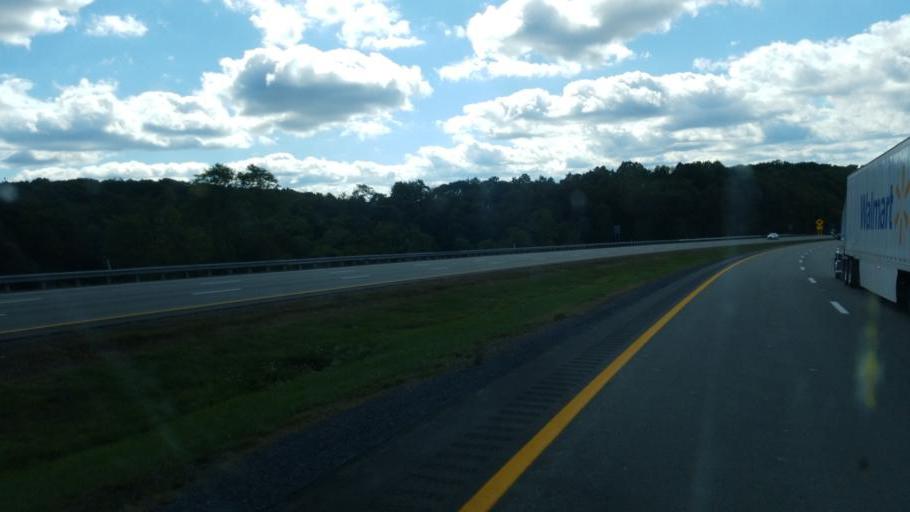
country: US
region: West Virginia
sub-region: Preston County
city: Terra Alta
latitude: 39.6601
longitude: -79.4962
